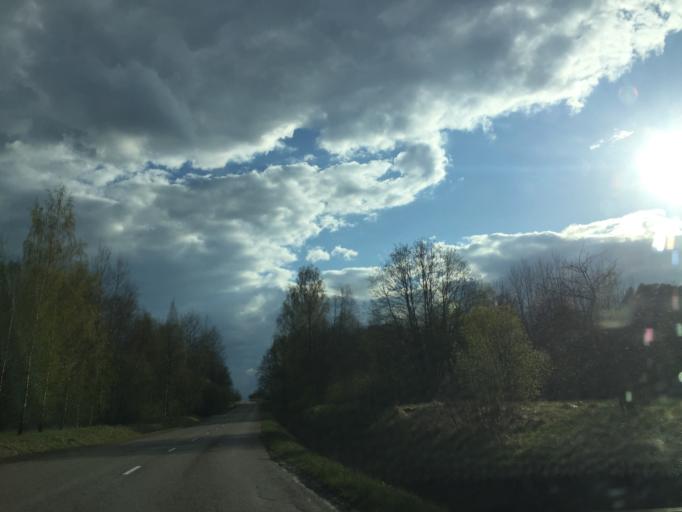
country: LV
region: Priekuli
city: Priekuli
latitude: 57.3848
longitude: 25.4380
